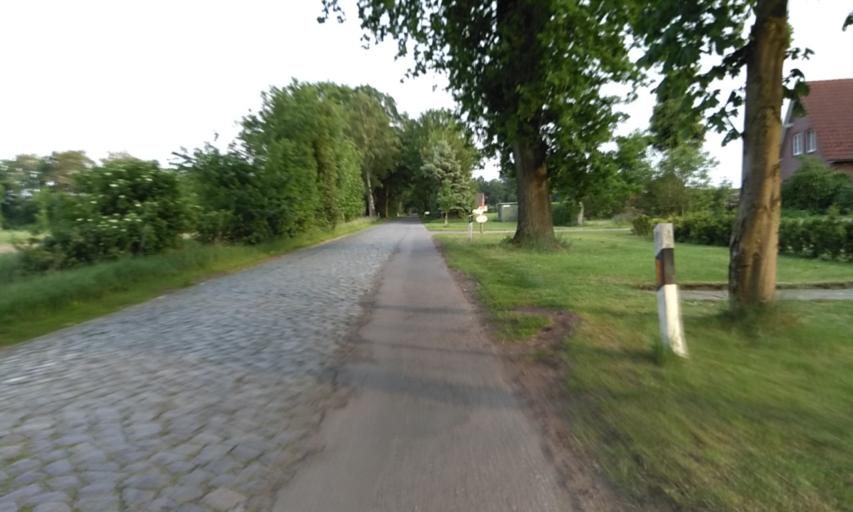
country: DE
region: Lower Saxony
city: Deinste
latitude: 53.5141
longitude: 9.4478
